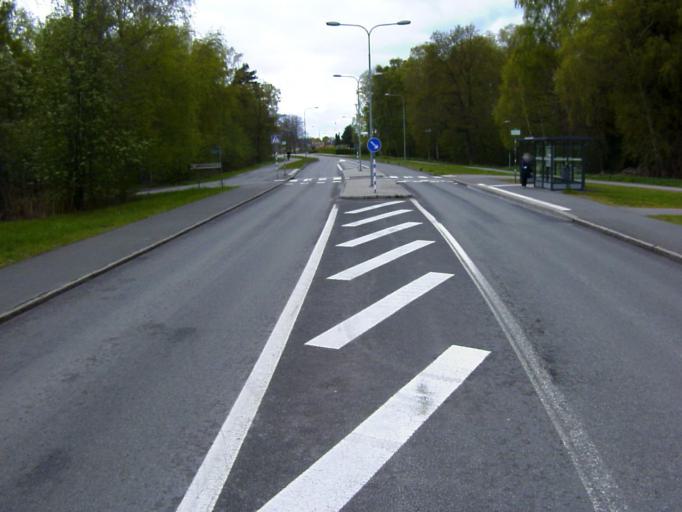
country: SE
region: Skane
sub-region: Kristianstads Kommun
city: Kristianstad
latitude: 56.0404
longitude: 14.1746
